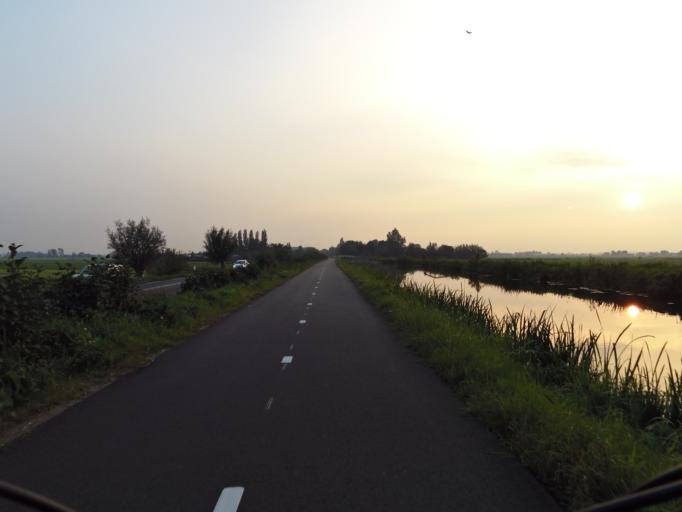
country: NL
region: South Holland
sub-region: Gemeente Voorschoten
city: Voorschoten
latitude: 52.1055
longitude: 4.4876
